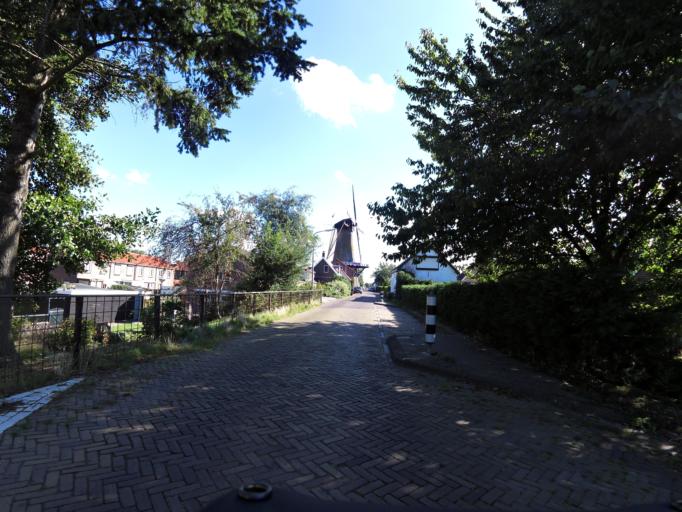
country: NL
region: South Holland
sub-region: Gemeente Zwijndrecht
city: Zwijndrecht
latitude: 51.7831
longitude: 4.6151
